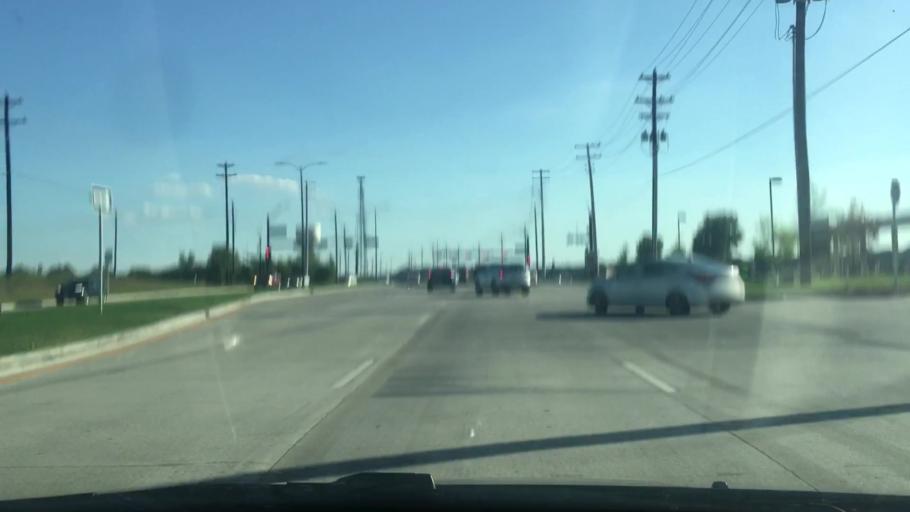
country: US
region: Texas
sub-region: Denton County
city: Little Elm
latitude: 33.1935
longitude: -96.8855
